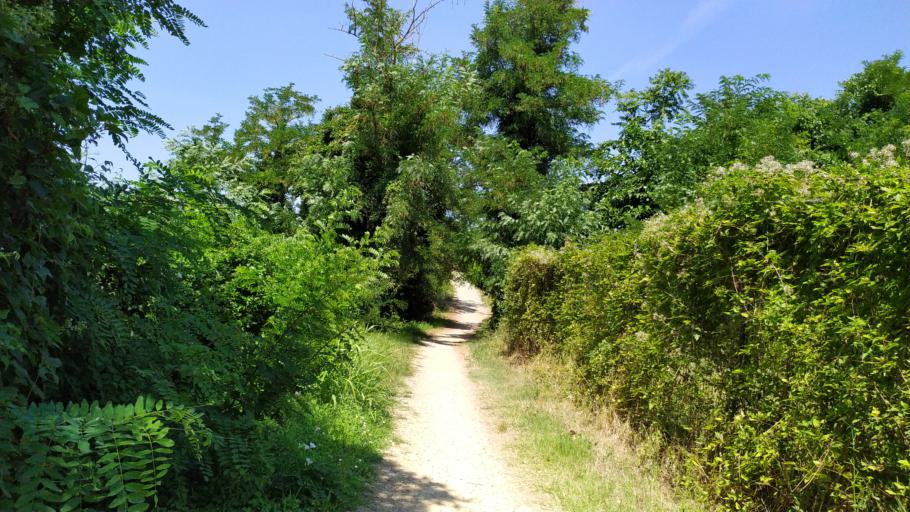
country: IT
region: Emilia-Romagna
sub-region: Forli-Cesena
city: Castrocaro Terme e Terra del Sole
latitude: 44.2041
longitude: 12.0046
